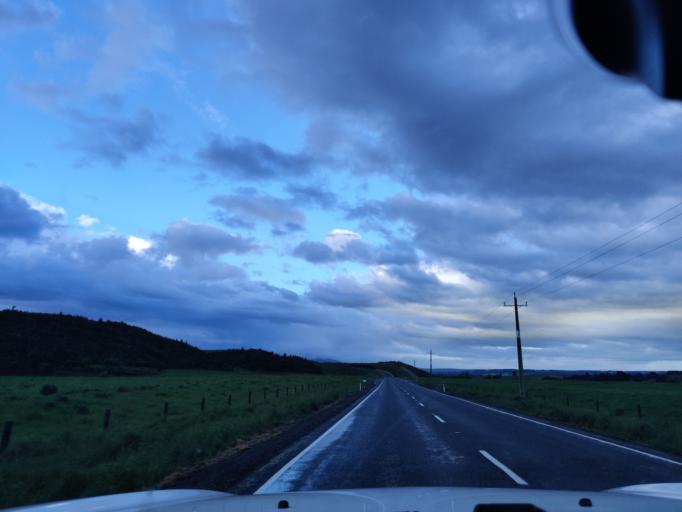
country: NZ
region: Waikato
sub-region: South Waikato District
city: Tokoroa
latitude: -38.3806
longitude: 175.7868
